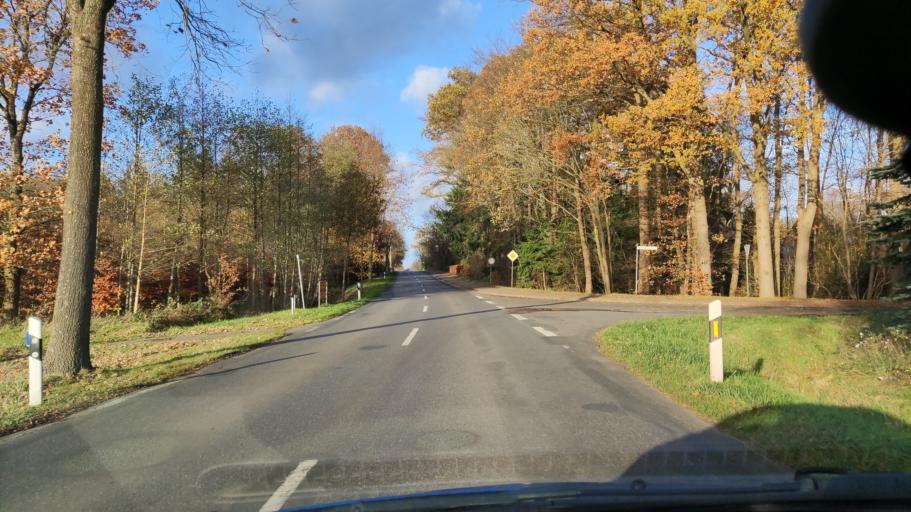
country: DE
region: Lower Saxony
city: Soltau
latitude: 53.0332
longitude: 9.8285
